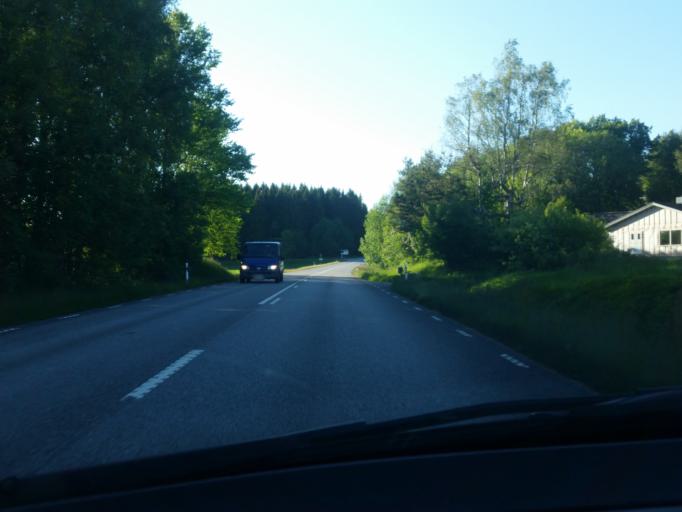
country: SE
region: Vaestra Goetaland
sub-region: Fargelanda Kommun
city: Faergelanda
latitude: 58.5177
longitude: 11.9824
